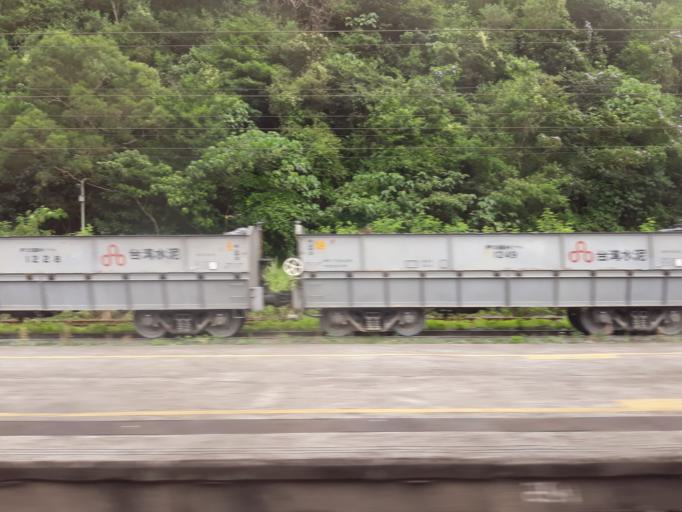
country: TW
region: Taiwan
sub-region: Yilan
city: Yilan
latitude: 24.5688
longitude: 121.8445
